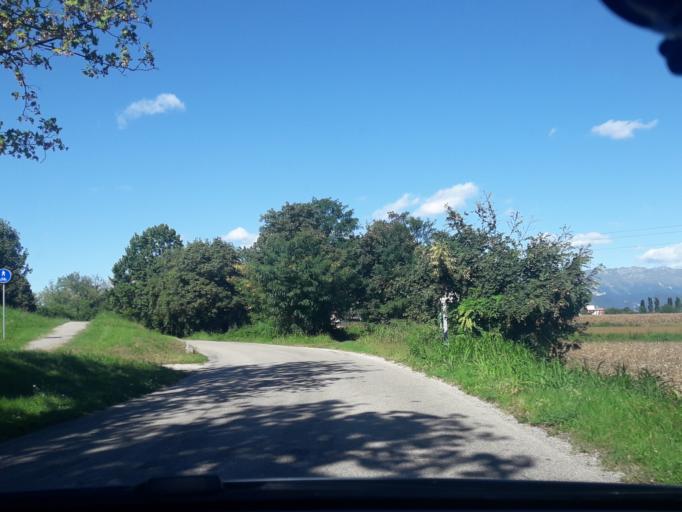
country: IT
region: Friuli Venezia Giulia
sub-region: Provincia di Udine
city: Reana del Roiale
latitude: 46.1370
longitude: 13.2167
